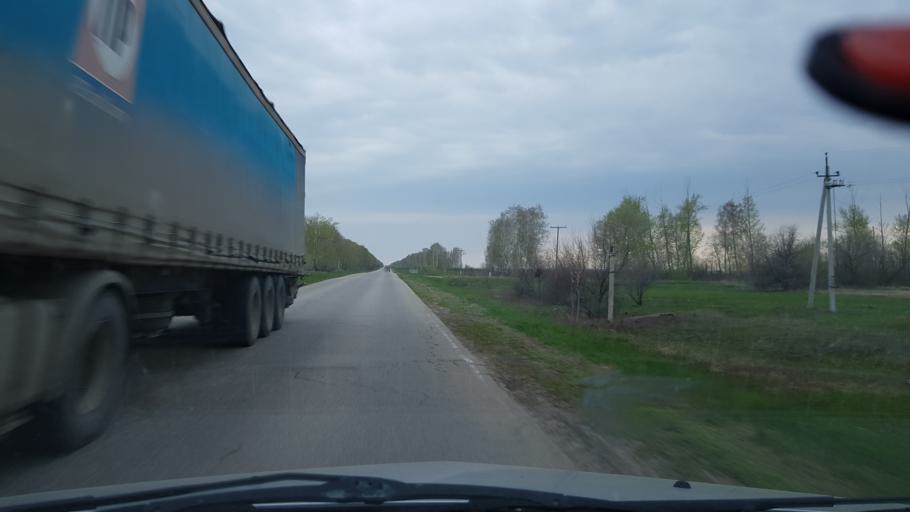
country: RU
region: Samara
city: Tol'yatti
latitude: 53.6583
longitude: 49.2431
